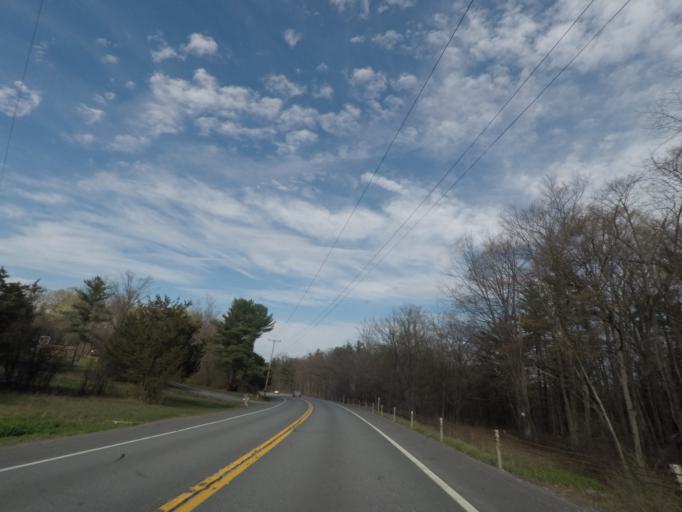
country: US
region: New York
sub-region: Albany County
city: Voorheesville
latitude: 42.5939
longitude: -73.9752
